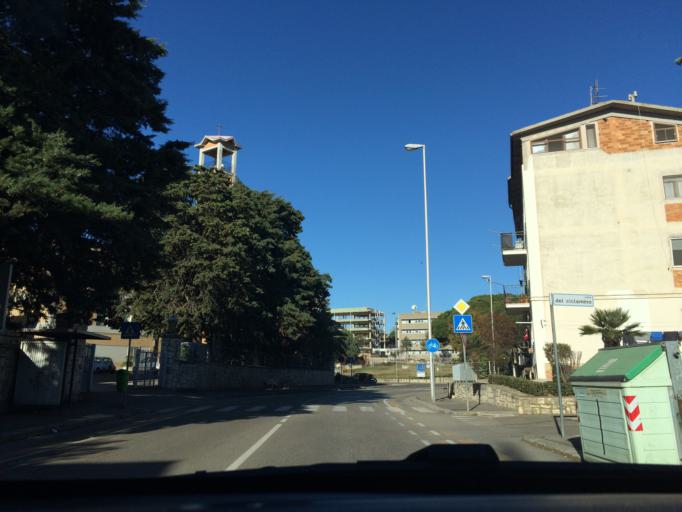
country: IT
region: Basilicate
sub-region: Provincia di Matera
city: Matera
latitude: 40.6596
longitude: 16.6015
